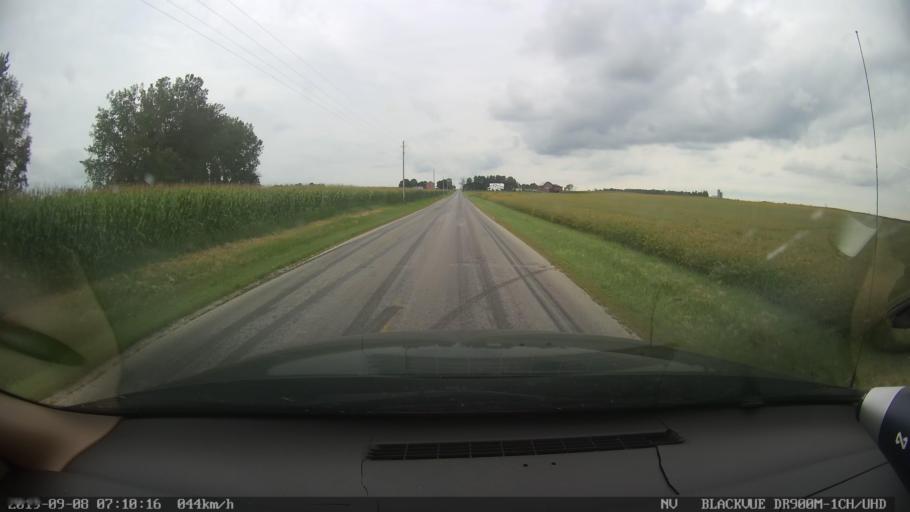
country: US
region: Ohio
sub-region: Richland County
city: Shelby
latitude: 40.9085
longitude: -82.6760
